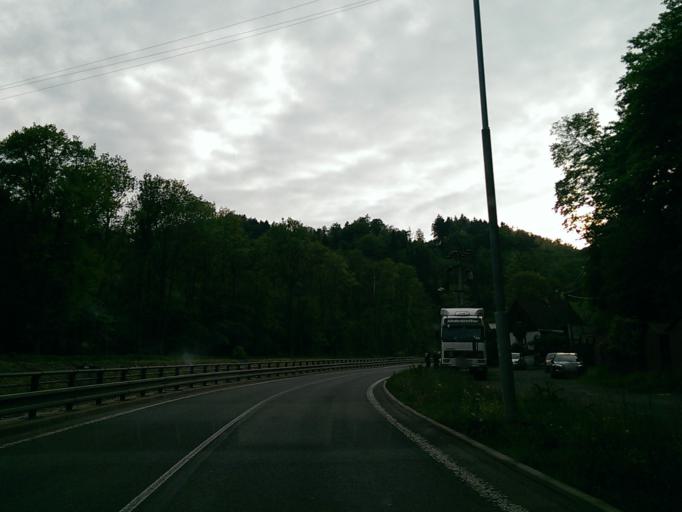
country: CZ
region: Liberecky
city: Zelezny Brod
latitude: 50.6408
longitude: 15.2431
